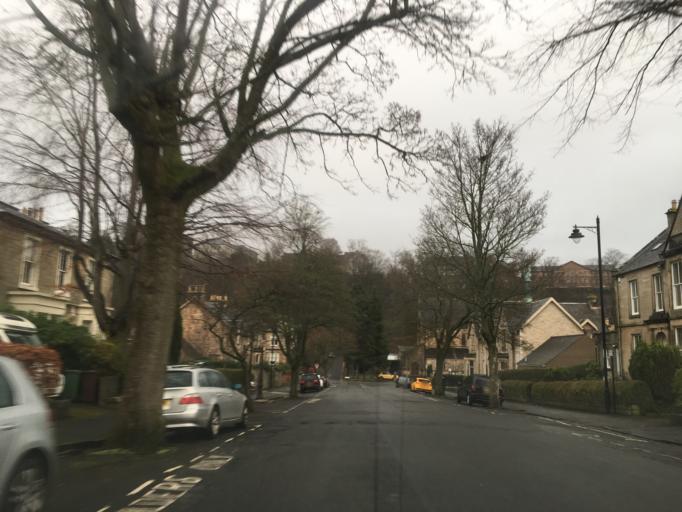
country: GB
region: Scotland
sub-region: Stirling
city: Stirling
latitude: 56.1173
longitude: -3.9440
